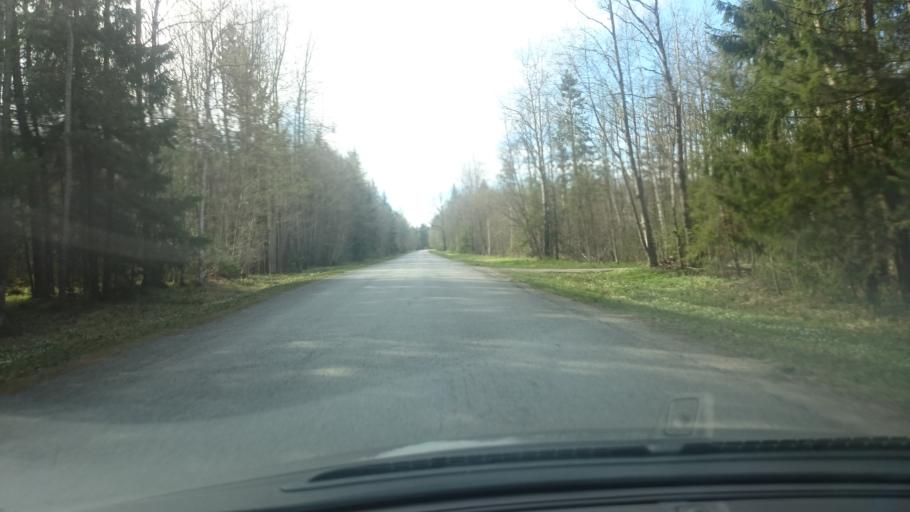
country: EE
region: Ida-Virumaa
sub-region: Sillamaee linn
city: Sillamae
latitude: 59.0817
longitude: 27.6802
